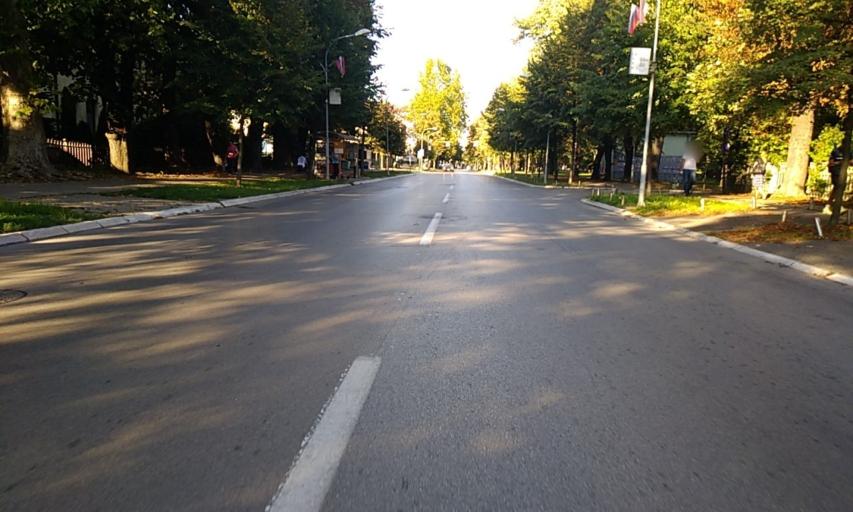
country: BA
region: Republika Srpska
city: Banja Luka
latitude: 44.7796
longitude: 17.1985
